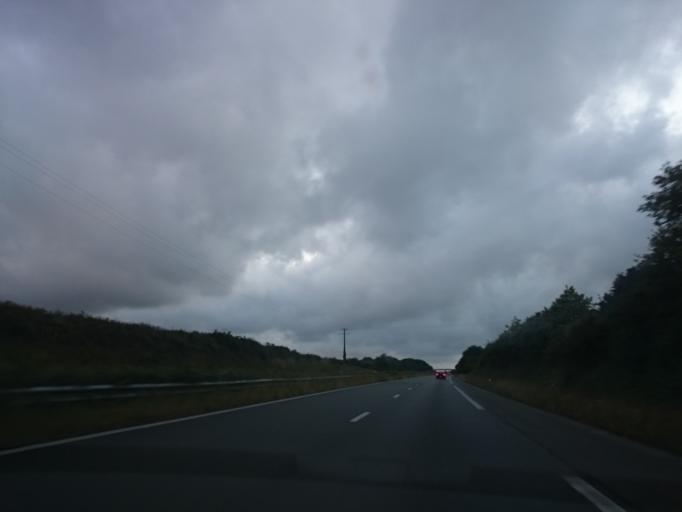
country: FR
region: Brittany
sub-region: Departement du Finistere
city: Pont-Aven
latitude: 47.8851
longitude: -3.7544
